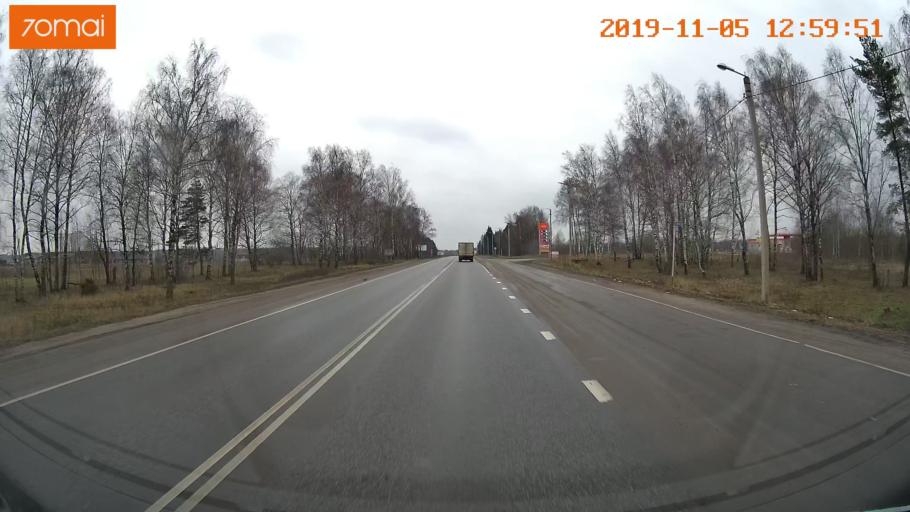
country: RU
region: Ivanovo
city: Kokhma
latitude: 56.9164
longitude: 41.1362
